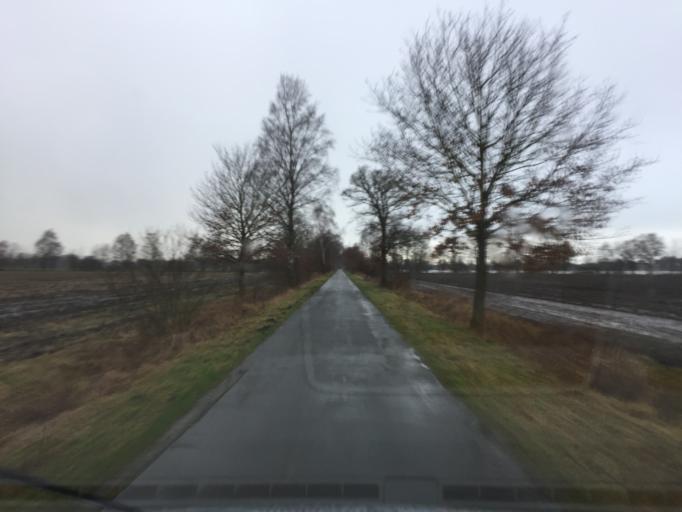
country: DE
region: Lower Saxony
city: Hassel
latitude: 52.6579
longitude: 8.8434
